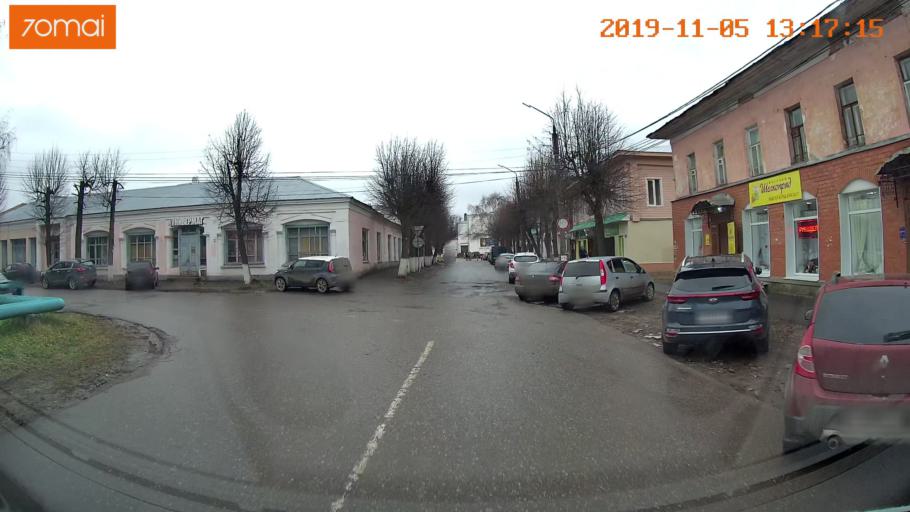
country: RU
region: Ivanovo
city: Shuya
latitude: 56.8545
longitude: 41.3784
